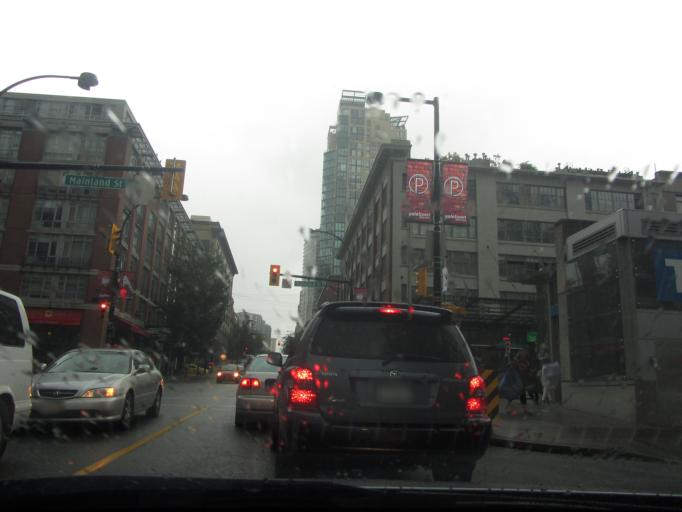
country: CA
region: British Columbia
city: West End
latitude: 49.2744
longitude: -123.1219
